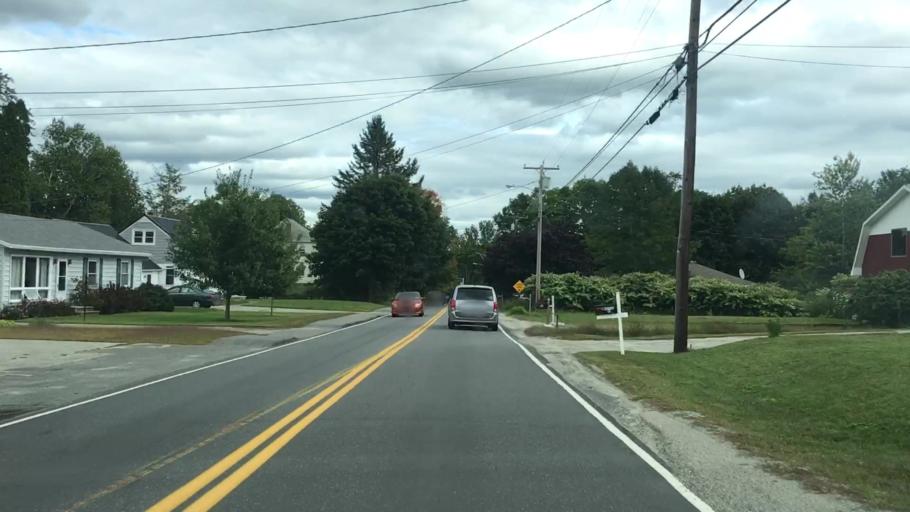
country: US
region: Maine
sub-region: Kennebec County
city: Hallowell
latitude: 44.2668
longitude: -69.7961
